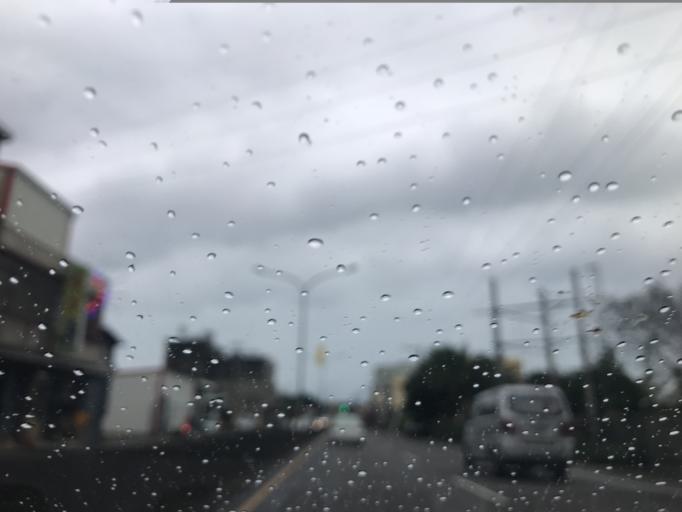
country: TW
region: Taiwan
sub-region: Hsinchu
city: Zhubei
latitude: 24.8268
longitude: 121.0512
